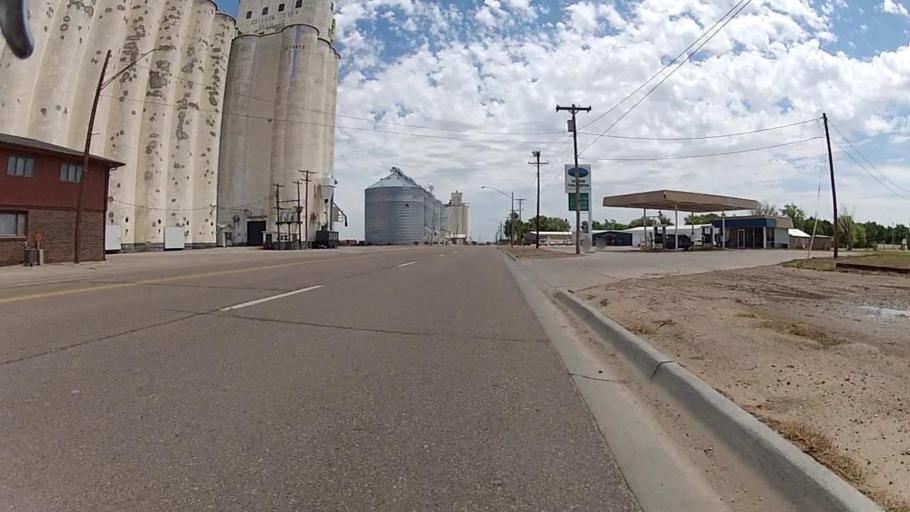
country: US
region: Kansas
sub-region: Haskell County
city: Satanta
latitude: 37.4384
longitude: -100.9918
